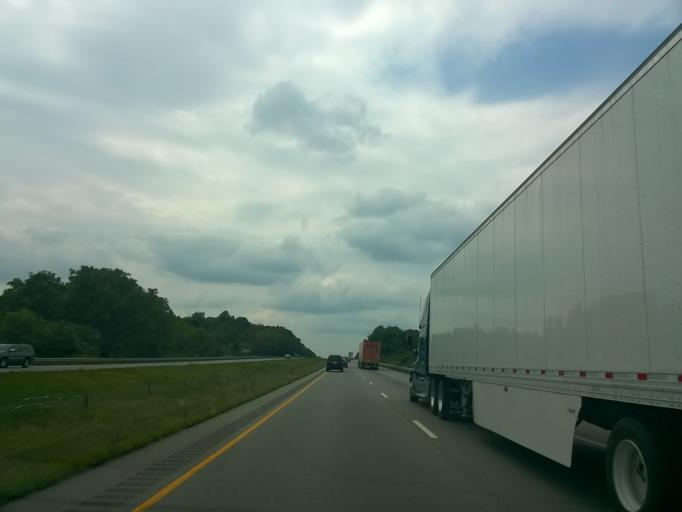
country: US
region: Indiana
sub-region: Putnam County
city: Cloverdale
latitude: 39.5347
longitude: -86.7836
